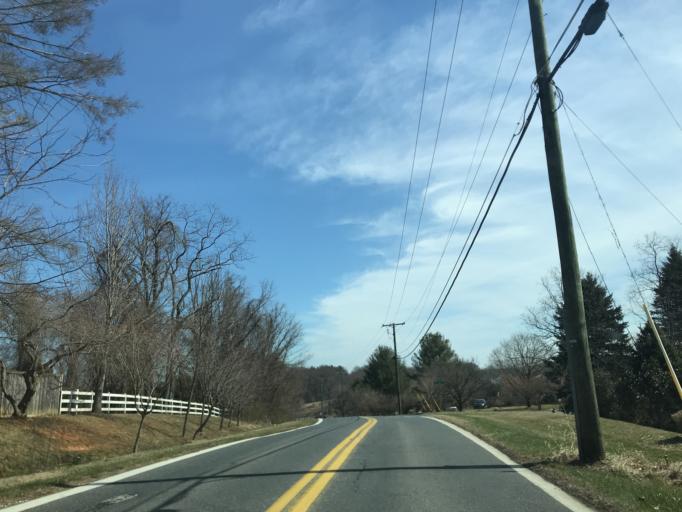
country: US
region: Maryland
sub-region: Montgomery County
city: Spencerville
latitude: 39.1422
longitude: -76.9694
